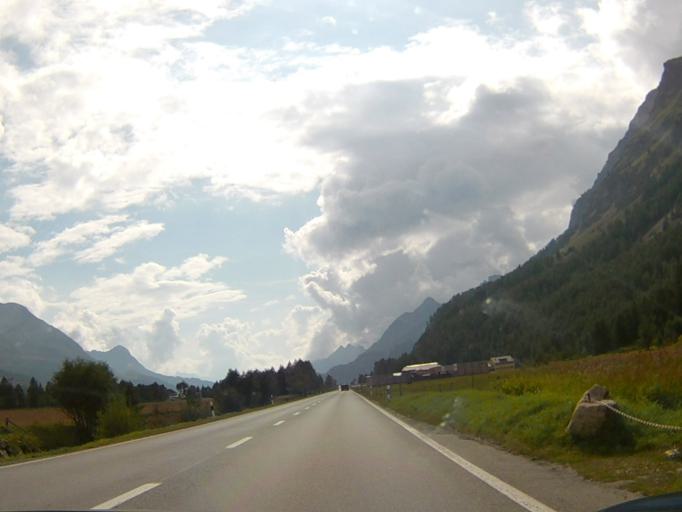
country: CH
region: Grisons
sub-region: Maloja District
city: Silvaplana
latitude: 46.4423
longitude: 9.7743
